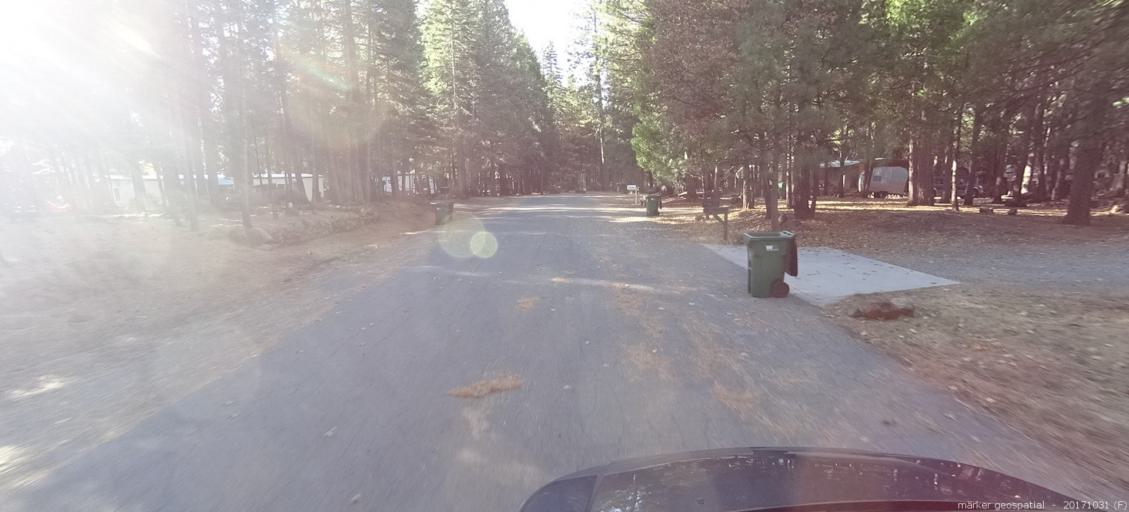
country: US
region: California
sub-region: Shasta County
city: Shingletown
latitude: 40.4990
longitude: -121.9073
